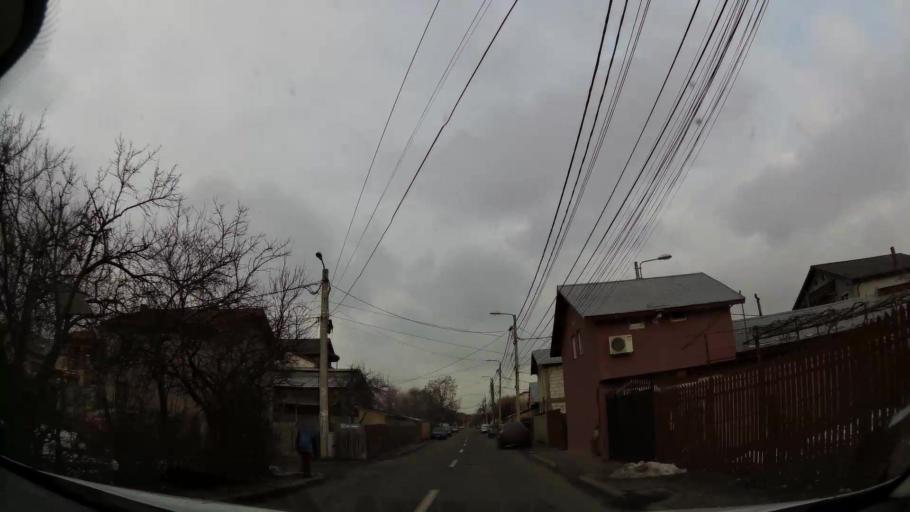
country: RO
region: Ilfov
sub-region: Voluntari City
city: Voluntari
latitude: 44.4933
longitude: 26.1658
